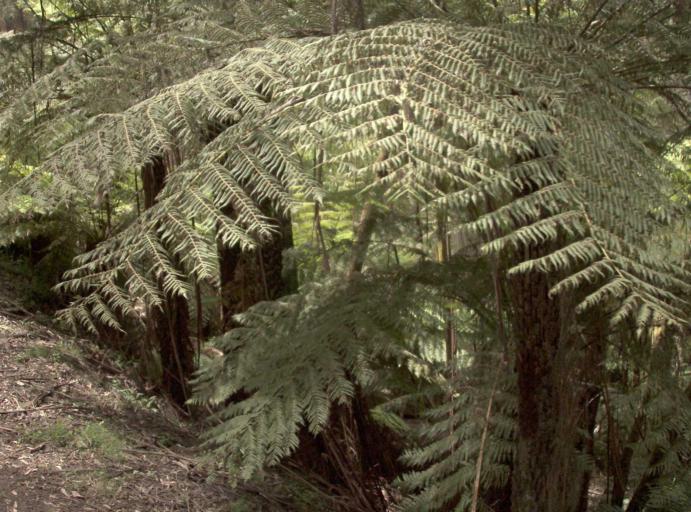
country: AU
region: Victoria
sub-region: Latrobe
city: Traralgon
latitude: -38.4450
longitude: 146.5365
